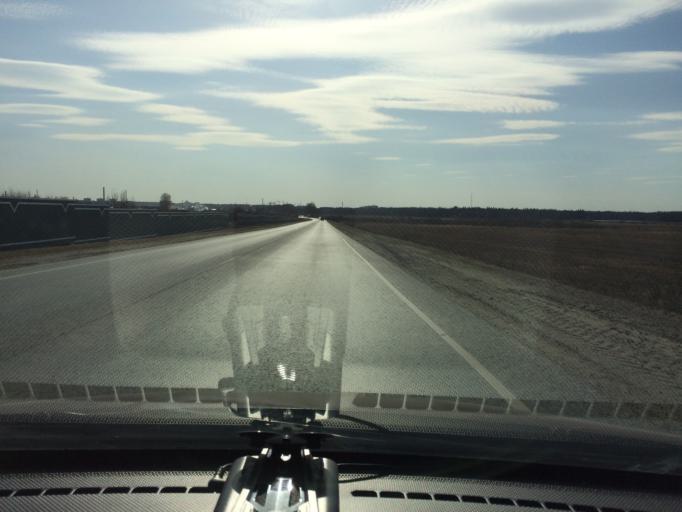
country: RU
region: Mariy-El
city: Yoshkar-Ola
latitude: 56.6575
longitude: 47.9656
